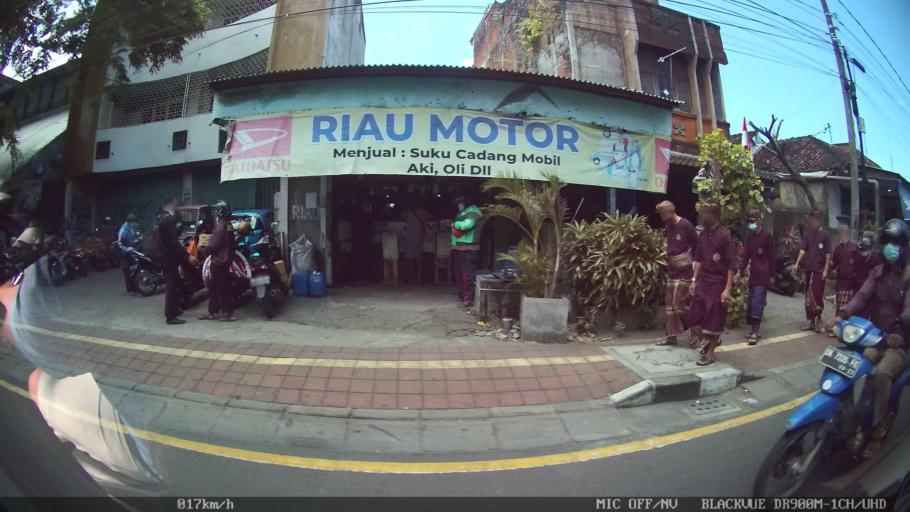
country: ID
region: Bali
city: Denpasar
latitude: -8.6589
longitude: 115.2096
